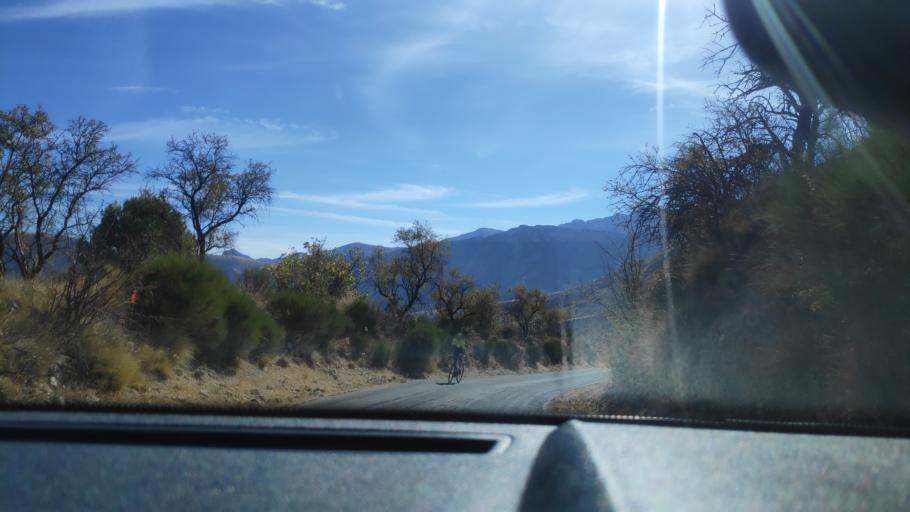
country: ES
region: Andalusia
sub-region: Provincia de Jaen
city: Torres
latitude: 37.7848
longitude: -3.4805
